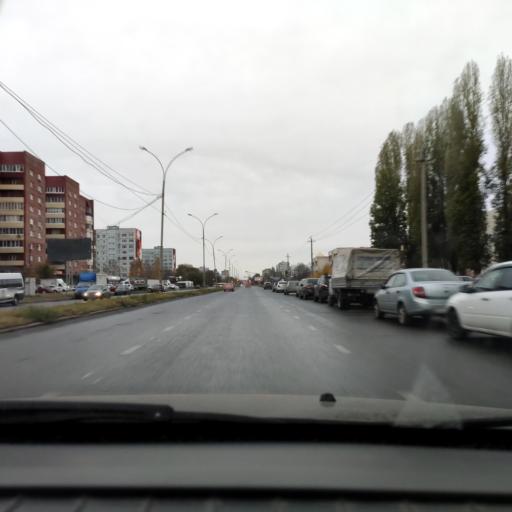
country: RU
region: Samara
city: Tol'yatti
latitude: 53.5392
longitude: 49.3149
